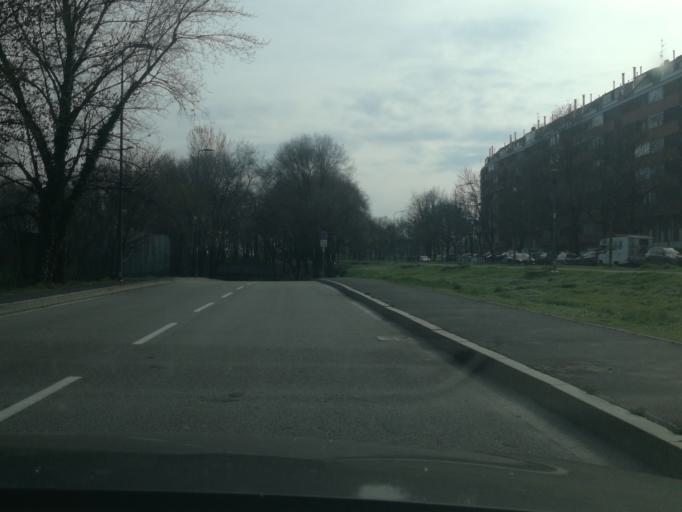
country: IT
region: Lombardy
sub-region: Citta metropolitana di Milano
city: Milano
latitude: 45.4330
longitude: 9.1650
